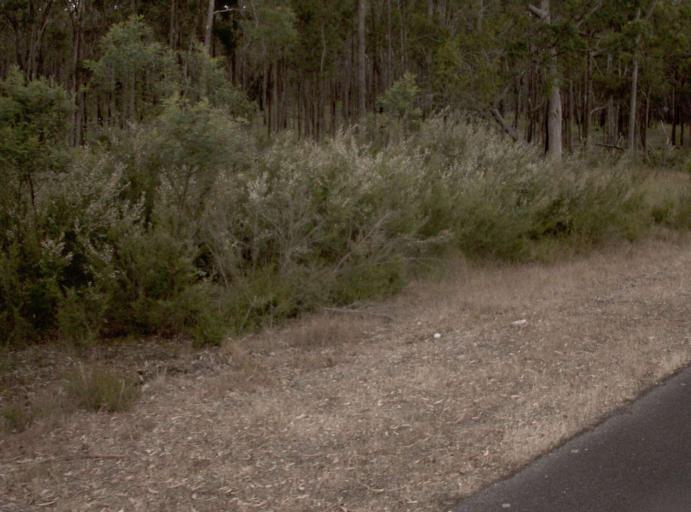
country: AU
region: Victoria
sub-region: Wellington
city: Sale
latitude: -38.4571
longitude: 146.9369
